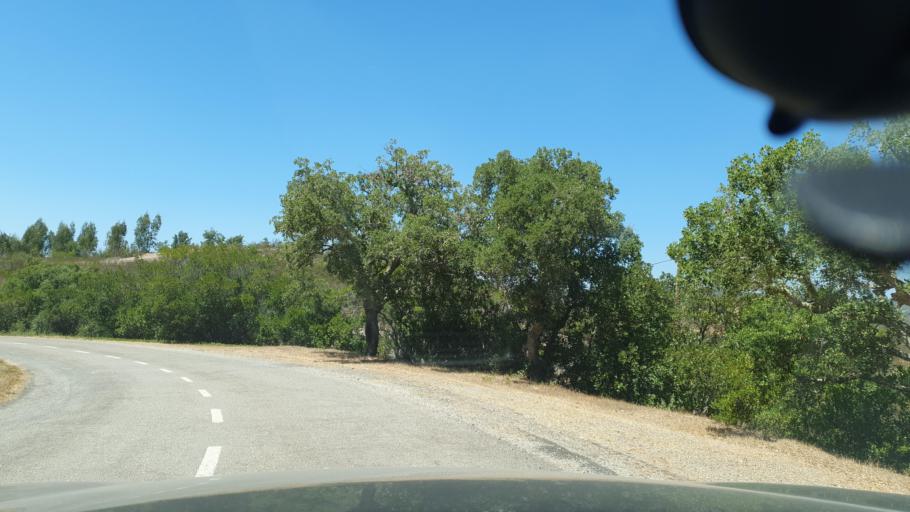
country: PT
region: Beja
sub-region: Odemira
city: Odemira
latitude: 37.5982
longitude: -8.5725
